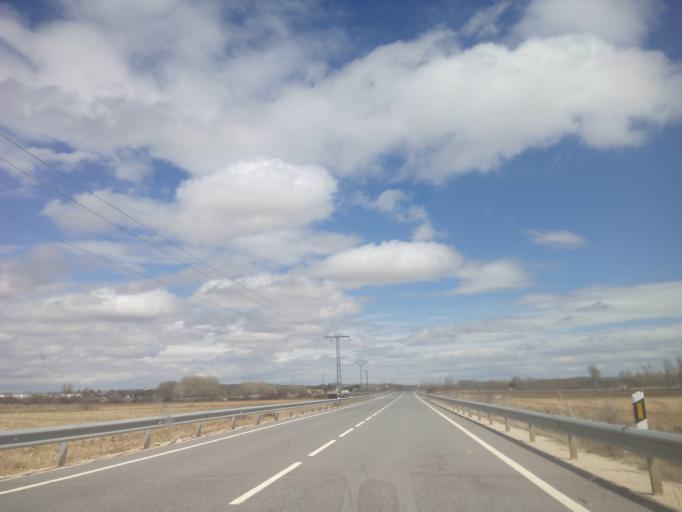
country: ES
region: Castille and Leon
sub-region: Provincia de Salamanca
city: Machacon
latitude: 40.9312
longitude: -5.5009
